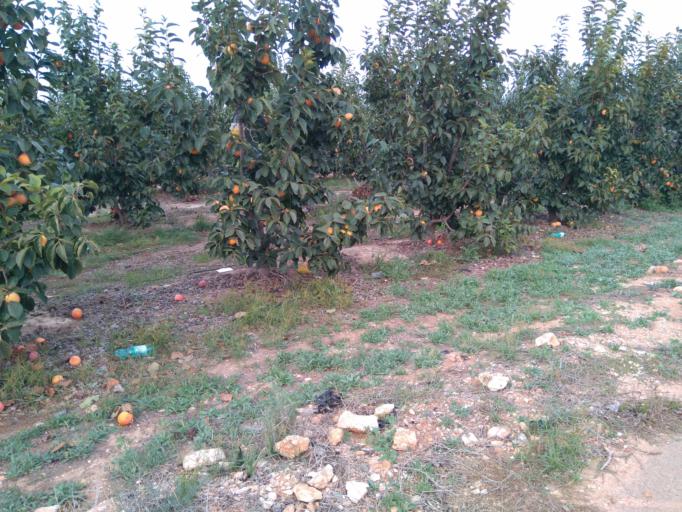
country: ES
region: Valencia
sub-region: Provincia de Valencia
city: Benimodo
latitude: 39.1999
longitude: -0.5825
